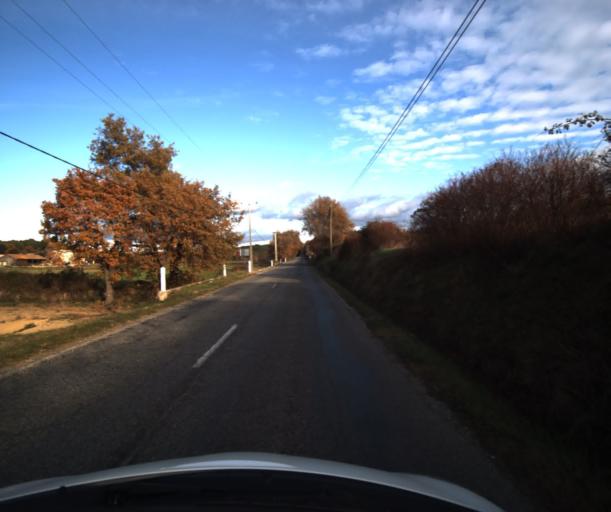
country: FR
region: Provence-Alpes-Cote d'Azur
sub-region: Departement du Vaucluse
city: Pertuis
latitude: 43.6961
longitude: 5.5369
